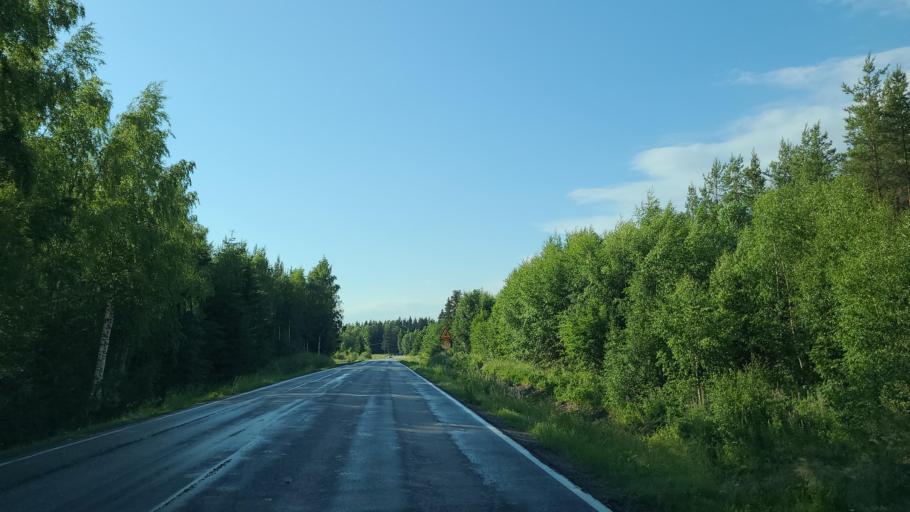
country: FI
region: Ostrobothnia
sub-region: Vaasa
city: Replot
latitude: 63.2149
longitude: 21.4280
